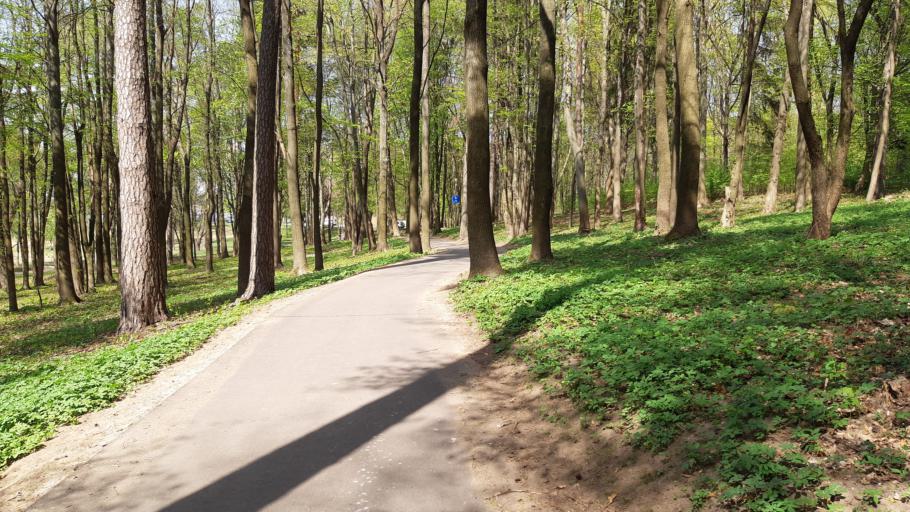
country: LT
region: Kauno apskritis
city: Dainava (Kaunas)
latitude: 54.8751
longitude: 24.0183
